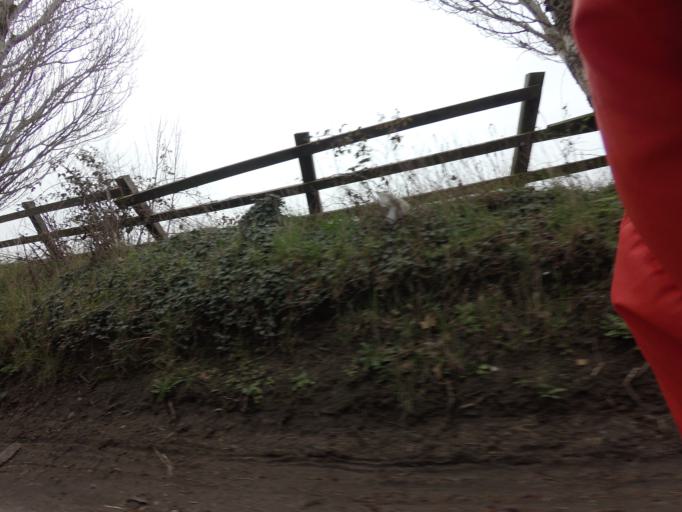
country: GB
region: England
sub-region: Kent
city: Swanley
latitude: 51.4000
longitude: 0.1475
